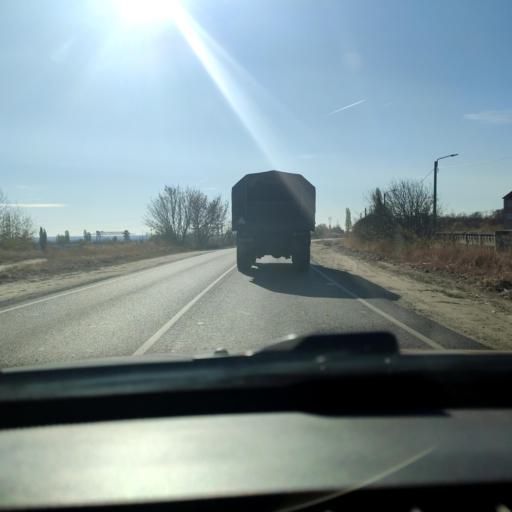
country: RU
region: Voronezj
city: Shilovo
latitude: 51.5662
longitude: 39.1403
